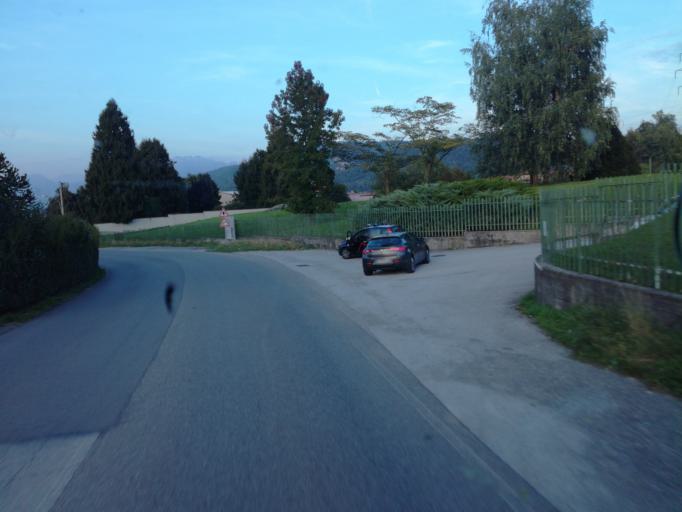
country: IT
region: Lombardy
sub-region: Provincia di Lecco
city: Sirtori
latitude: 45.7465
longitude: 9.3270
